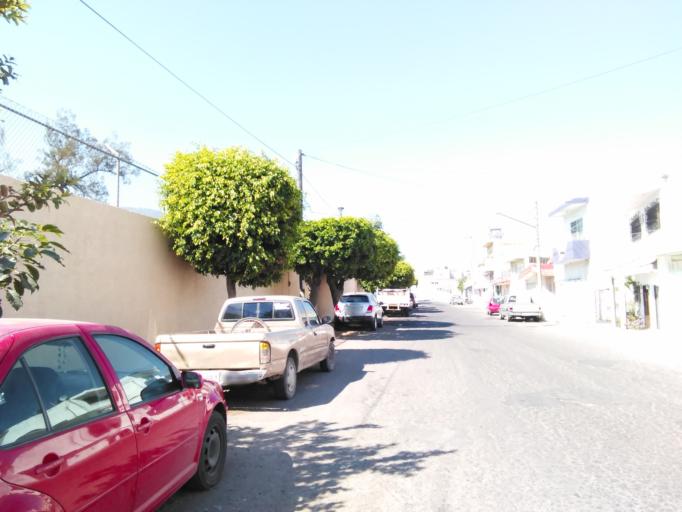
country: MX
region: Nayarit
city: Tepic
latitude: 21.4969
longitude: -104.8903
